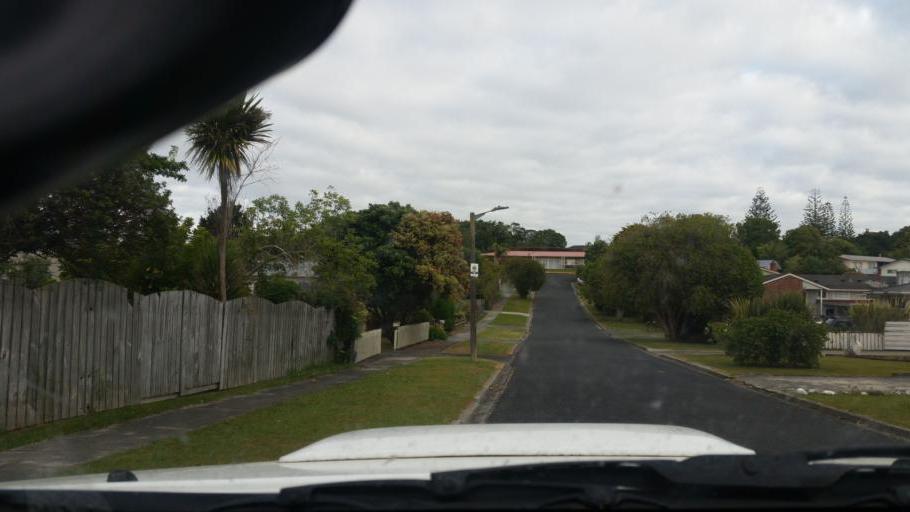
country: NZ
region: Northland
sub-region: Kaipara District
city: Dargaville
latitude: -35.9318
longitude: 173.8736
